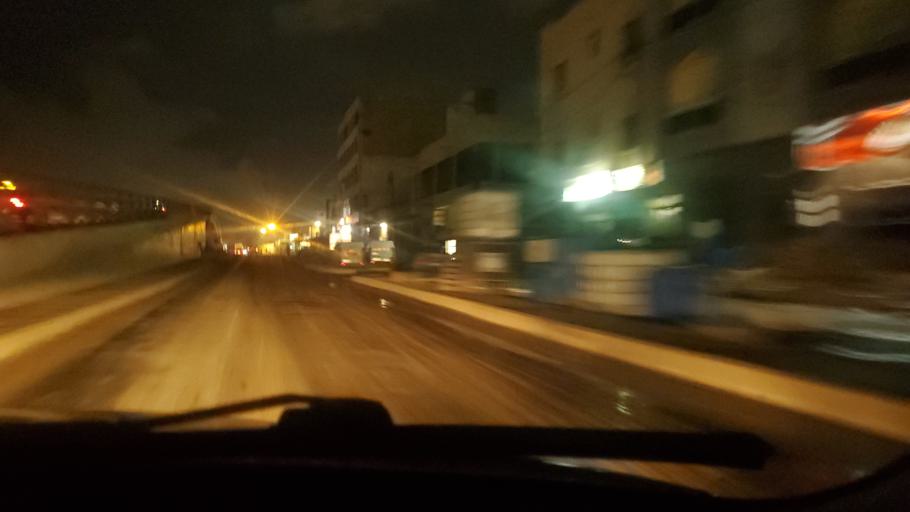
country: SN
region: Dakar
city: Pikine
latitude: 14.7453
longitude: -17.3790
